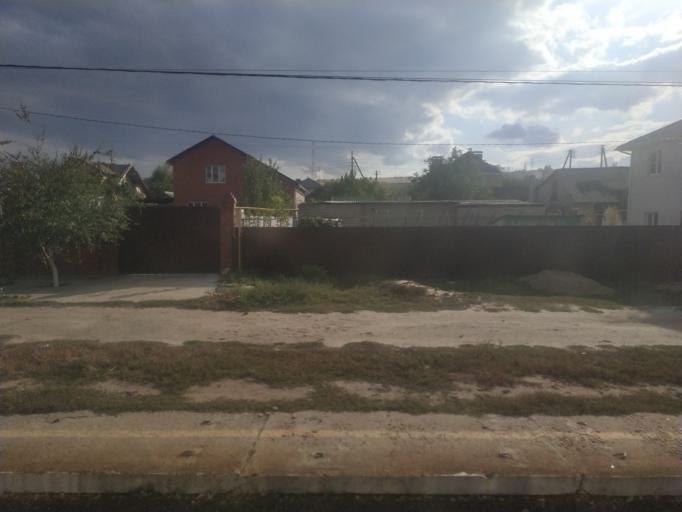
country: RU
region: Volgograd
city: Krasnoslobodsk
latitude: 48.5087
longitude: 44.5378
